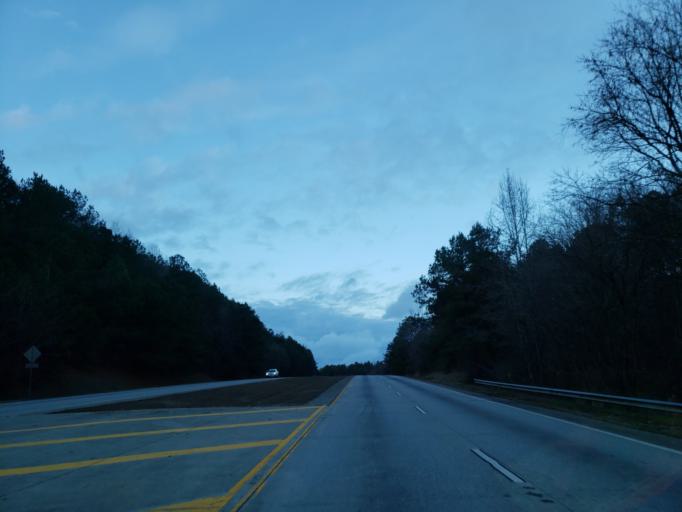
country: US
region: Georgia
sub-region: Fulton County
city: Union City
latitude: 33.6755
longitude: -84.5522
